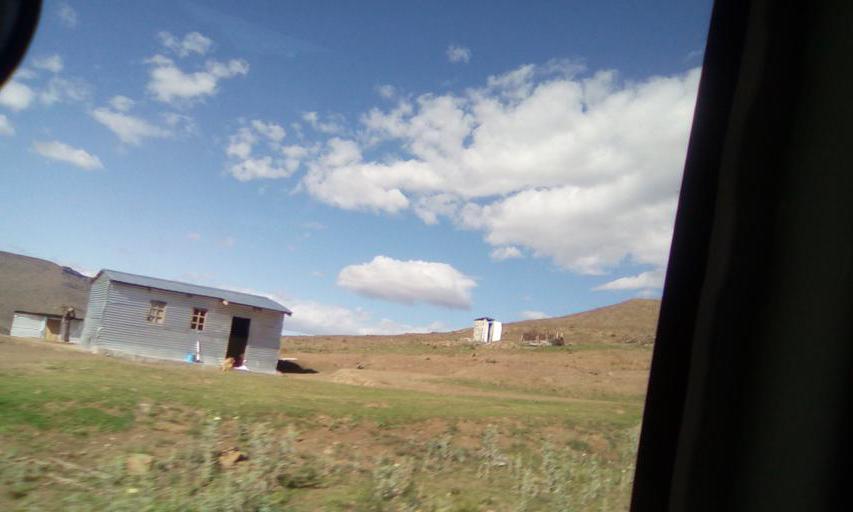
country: LS
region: Qacha's Nek
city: Qacha's Nek
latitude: -30.0244
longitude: 28.1754
